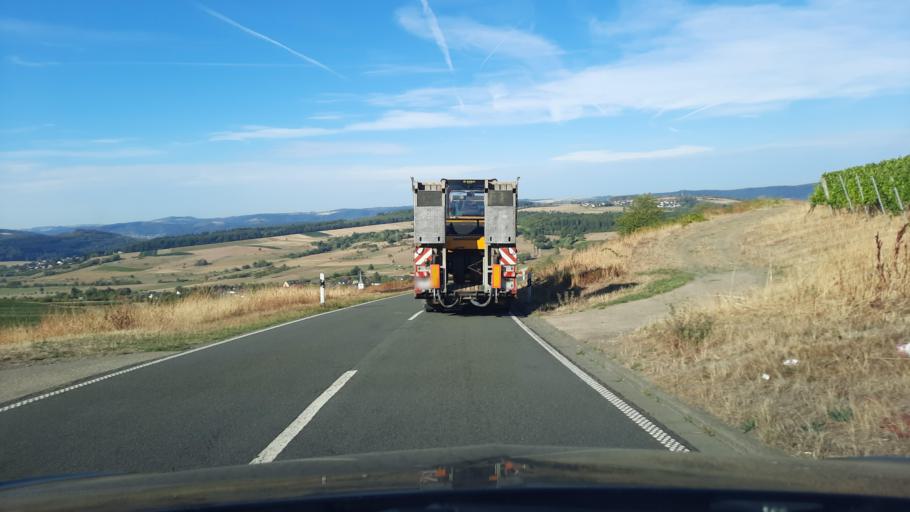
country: DE
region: Rheinland-Pfalz
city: Pellingen
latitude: 49.6834
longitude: 6.6502
